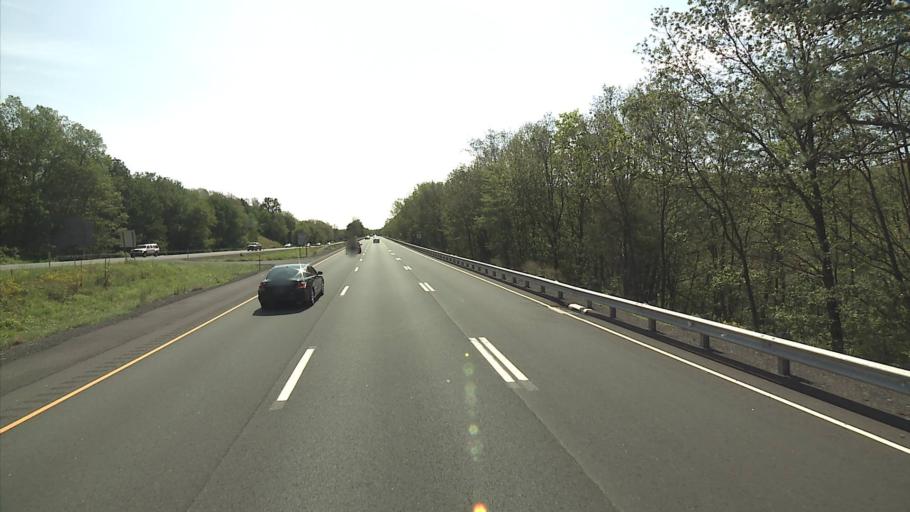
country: US
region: Connecticut
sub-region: Hartford County
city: Terramuggus
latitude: 41.6632
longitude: -72.5272
